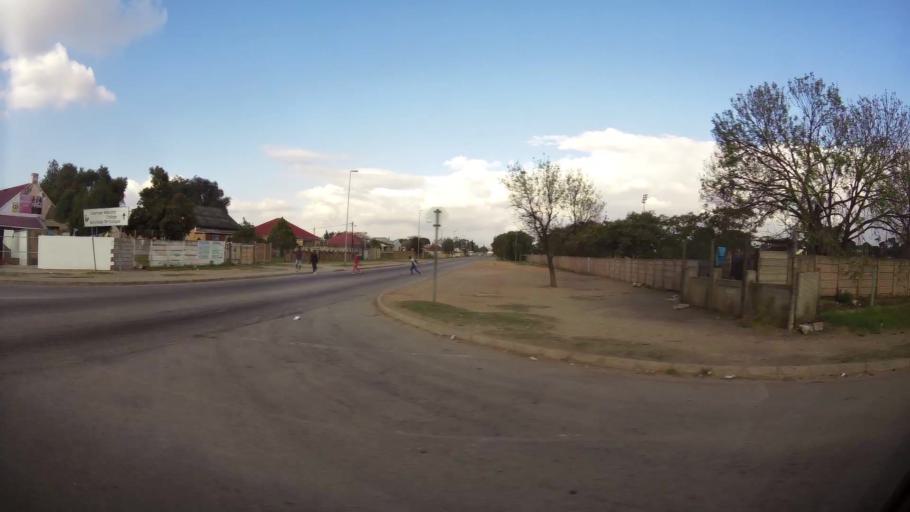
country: ZA
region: Eastern Cape
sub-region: Nelson Mandela Bay Metropolitan Municipality
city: Uitenhage
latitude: -33.7734
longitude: 25.3960
